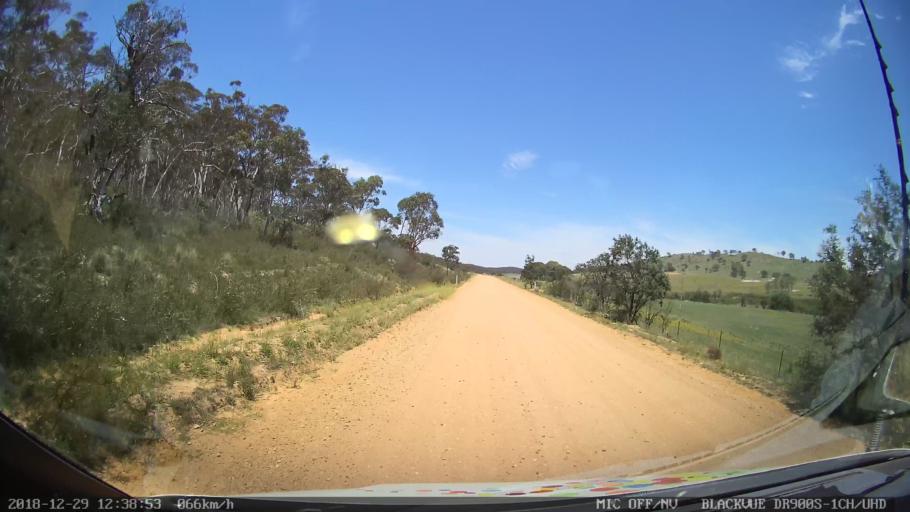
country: AU
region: Australian Capital Territory
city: Macarthur
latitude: -35.5928
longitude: 149.2283
